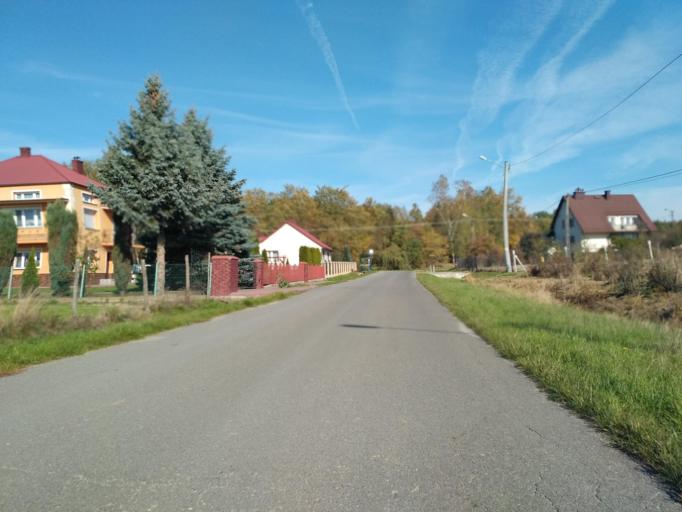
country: PL
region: Subcarpathian Voivodeship
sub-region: Powiat rzeszowski
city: Trzciana
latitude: 50.0869
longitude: 21.8137
